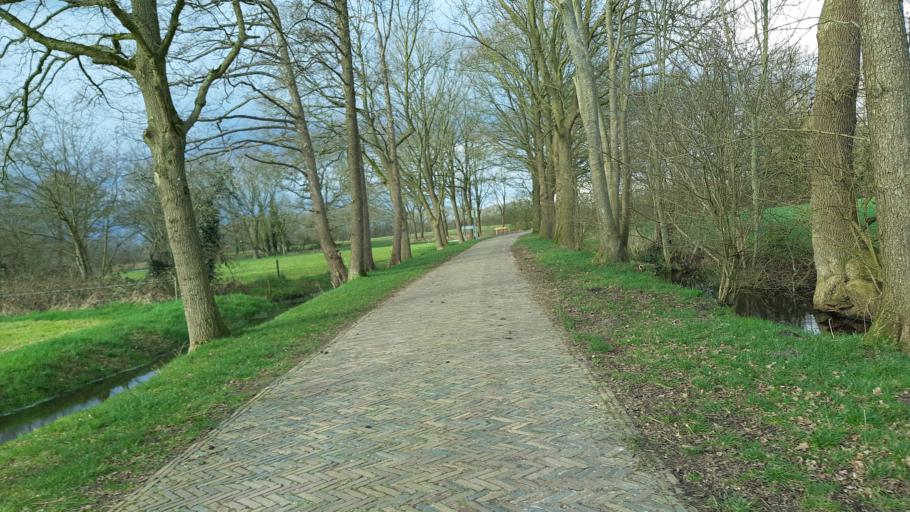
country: NL
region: Drenthe
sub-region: Gemeente Borger-Odoorn
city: Borger
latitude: 52.8453
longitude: 6.6583
